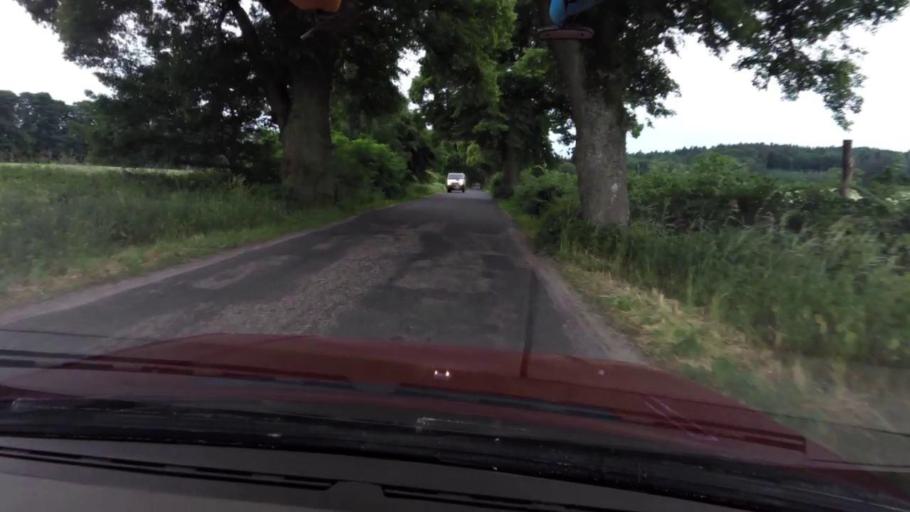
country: PL
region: Pomeranian Voivodeship
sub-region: Powiat slupski
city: Kepice
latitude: 54.2157
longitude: 16.8366
